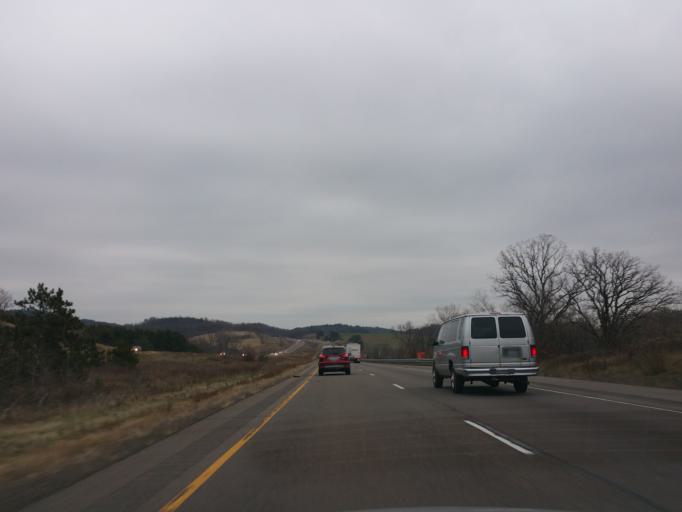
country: US
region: Wisconsin
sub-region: Trempealeau County
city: Osseo
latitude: 44.4916
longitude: -91.1216
